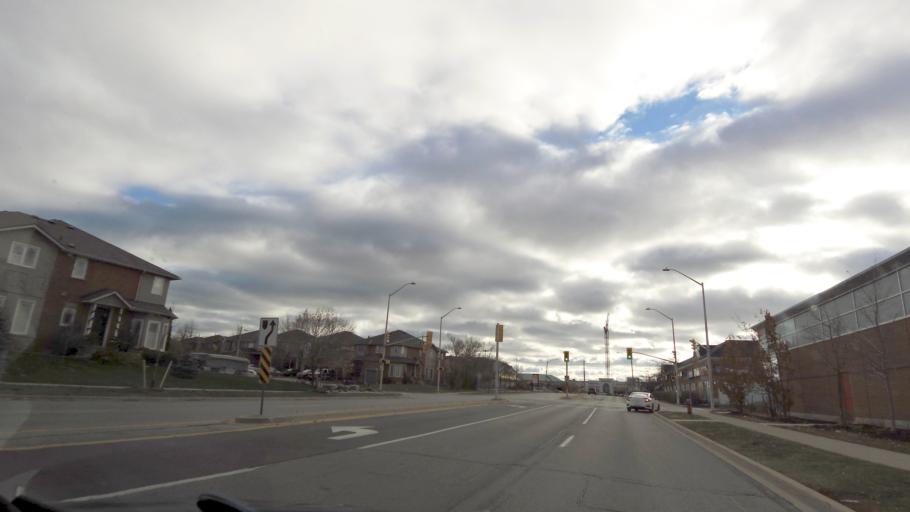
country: CA
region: Ontario
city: Oakville
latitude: 43.4860
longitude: -79.7134
